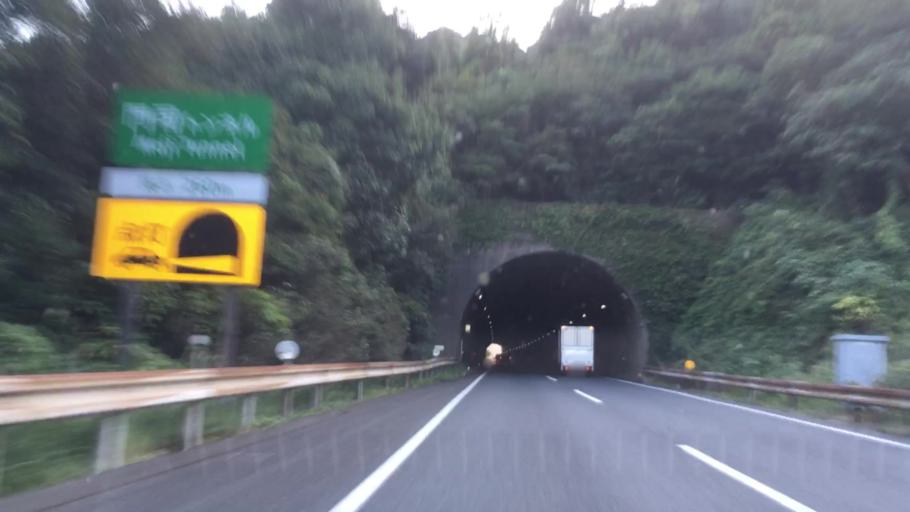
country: JP
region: Yamaguchi
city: Shimonoseki
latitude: 33.9188
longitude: 130.9785
